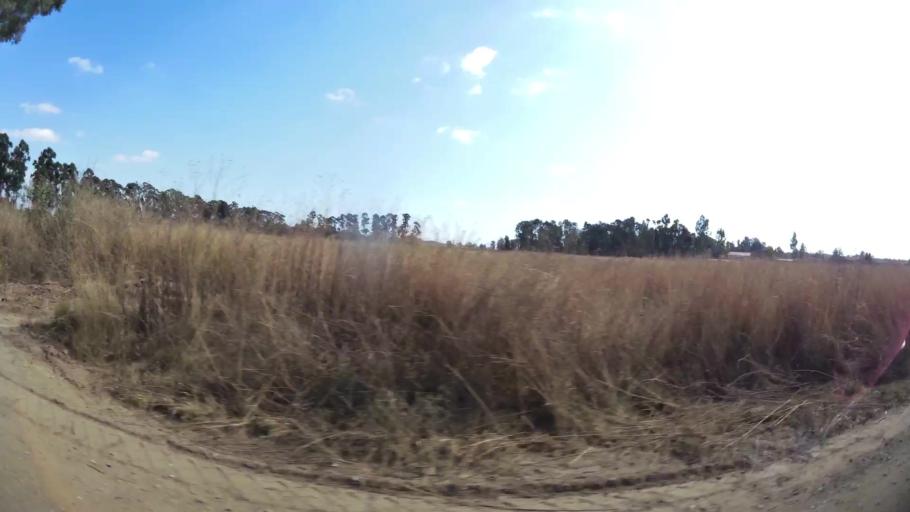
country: ZA
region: Gauteng
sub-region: Ekurhuleni Metropolitan Municipality
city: Benoni
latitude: -26.0849
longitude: 28.3685
